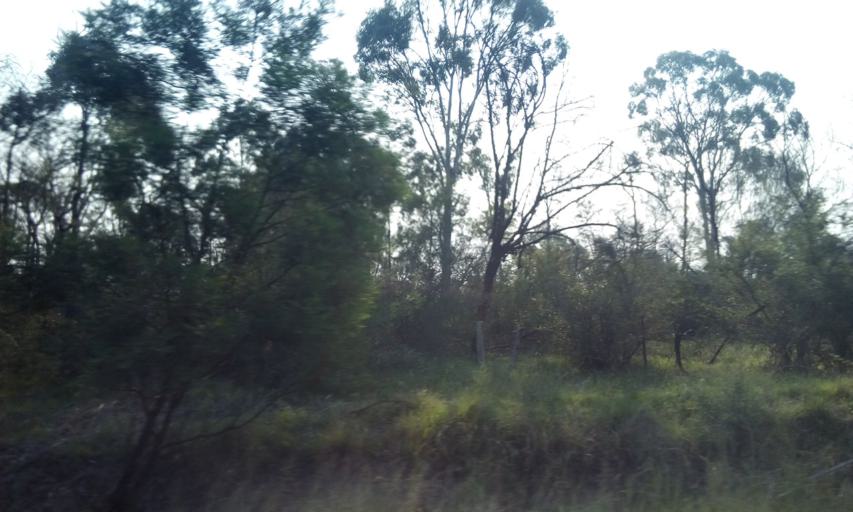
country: AU
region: New South Wales
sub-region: Wollondilly
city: Douglas Park
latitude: -34.2246
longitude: 150.7522
